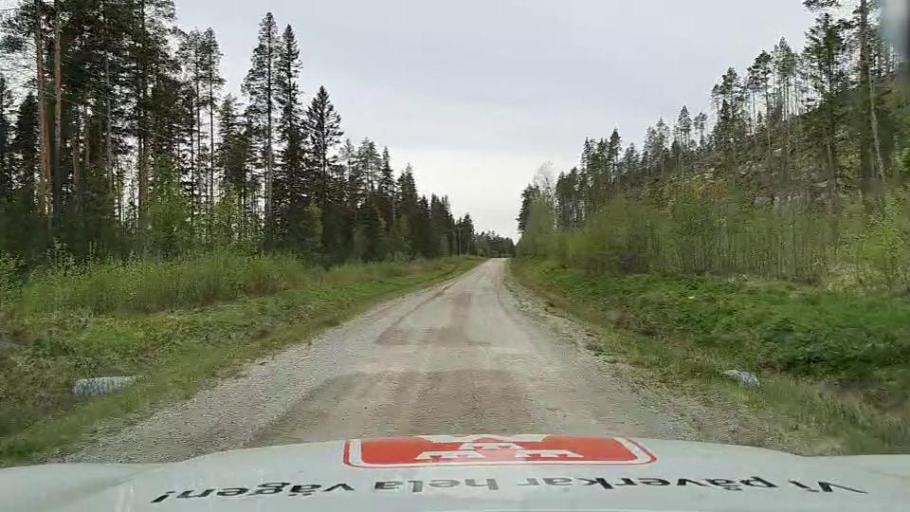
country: SE
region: Jaemtland
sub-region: Bergs Kommun
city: Hoverberg
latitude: 62.6715
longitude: 14.8056
